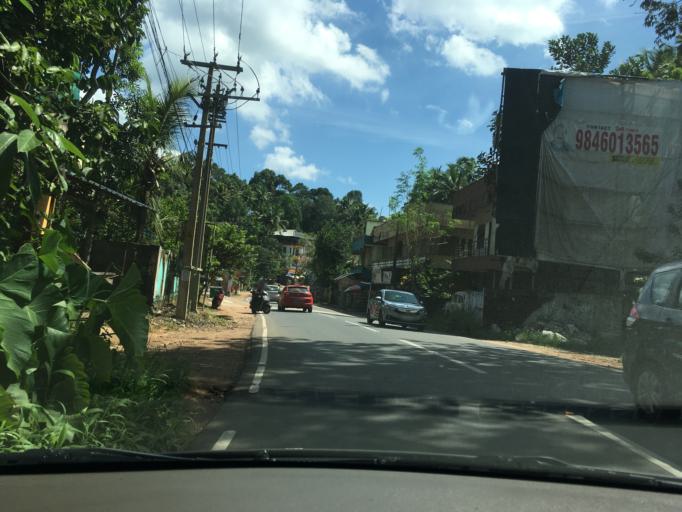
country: IN
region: Kerala
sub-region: Thiruvananthapuram
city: Nedumangad
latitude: 8.5826
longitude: 76.9947
